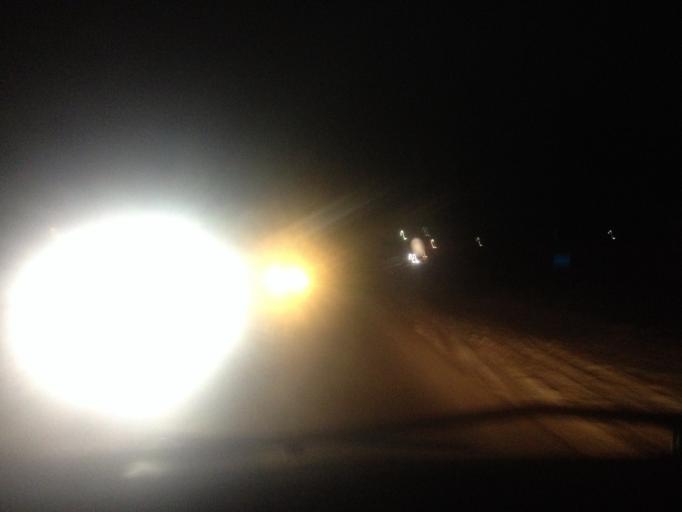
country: RU
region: Tula
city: Barsuki
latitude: 54.2728
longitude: 37.4783
